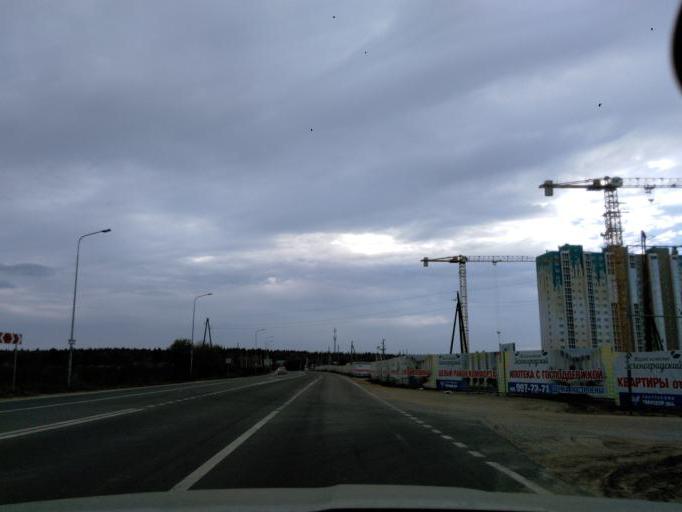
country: RU
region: Moskovskaya
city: Andreyevka
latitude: 55.9743
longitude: 37.1039
